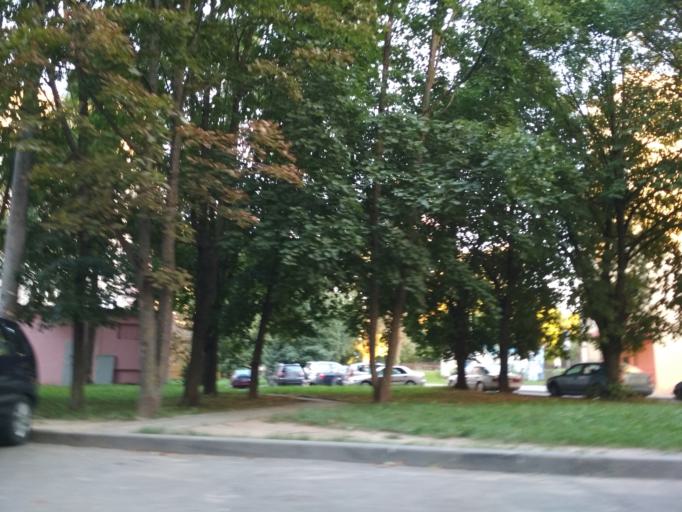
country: BY
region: Minsk
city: Minsk
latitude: 53.8809
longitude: 27.5368
